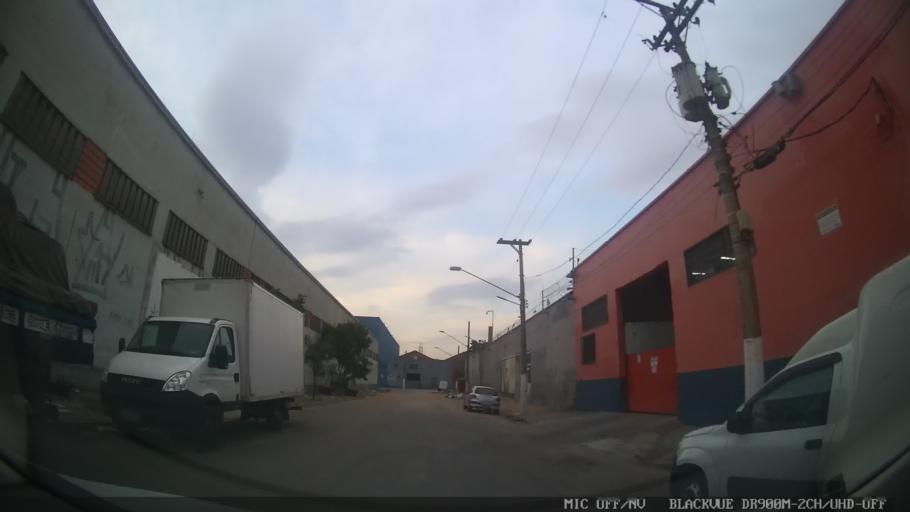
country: BR
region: Sao Paulo
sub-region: Sao Caetano Do Sul
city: Sao Caetano do Sul
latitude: -23.5980
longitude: -46.5881
